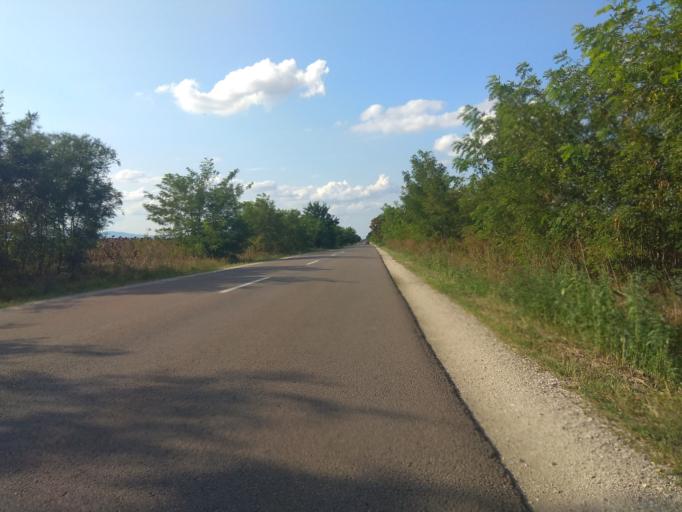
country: HU
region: Borsod-Abauj-Zemplen
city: Hejobaba
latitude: 47.9098
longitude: 20.8856
